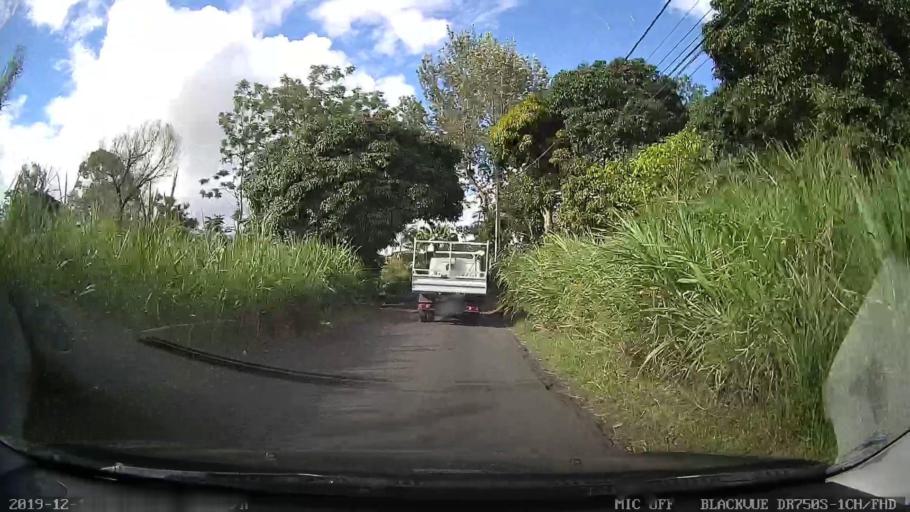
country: RE
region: Reunion
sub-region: Reunion
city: Le Tampon
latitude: -21.2537
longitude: 55.5111
